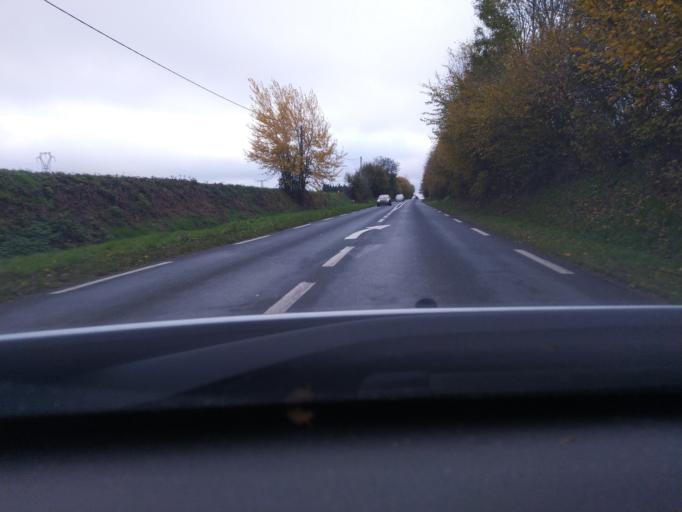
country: FR
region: Haute-Normandie
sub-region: Departement de la Seine-Maritime
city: La Vaupaliere
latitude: 49.4947
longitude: 0.9909
